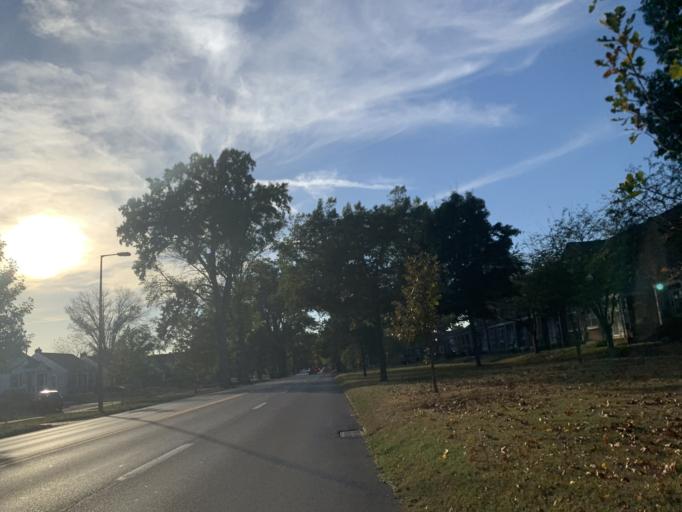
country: US
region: Kentucky
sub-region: Jefferson County
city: Shively
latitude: 38.2231
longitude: -85.7902
